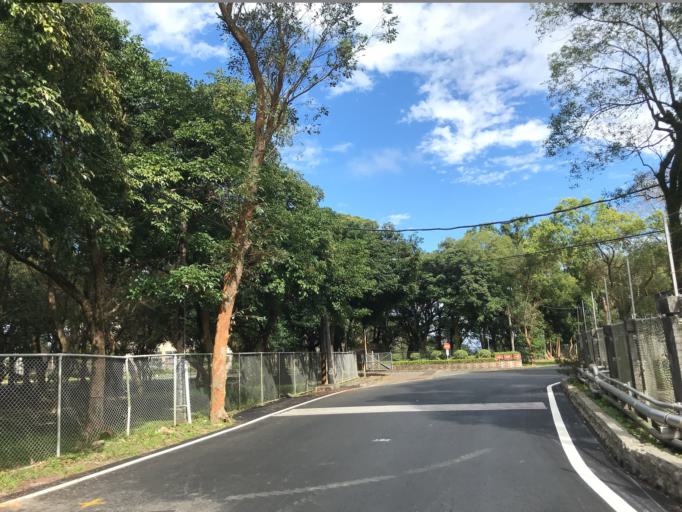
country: TW
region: Taiwan
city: Daxi
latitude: 24.8383
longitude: 121.2417
